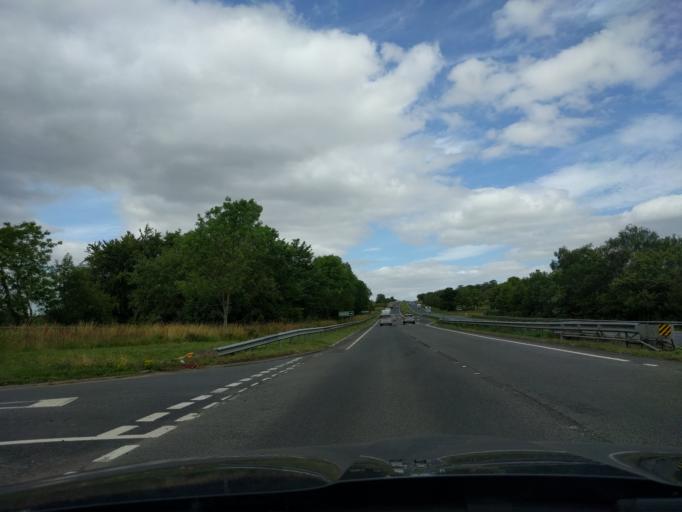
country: GB
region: England
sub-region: Northumberland
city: Alnwick
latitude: 55.3523
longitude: -1.7275
